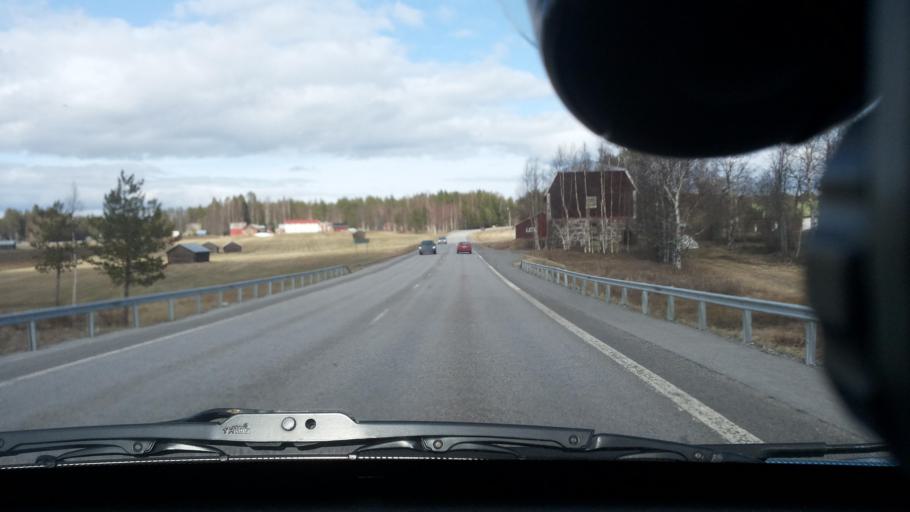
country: SE
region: Norrbotten
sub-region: Lulea Kommun
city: Gammelstad
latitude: 65.5903
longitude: 22.0362
